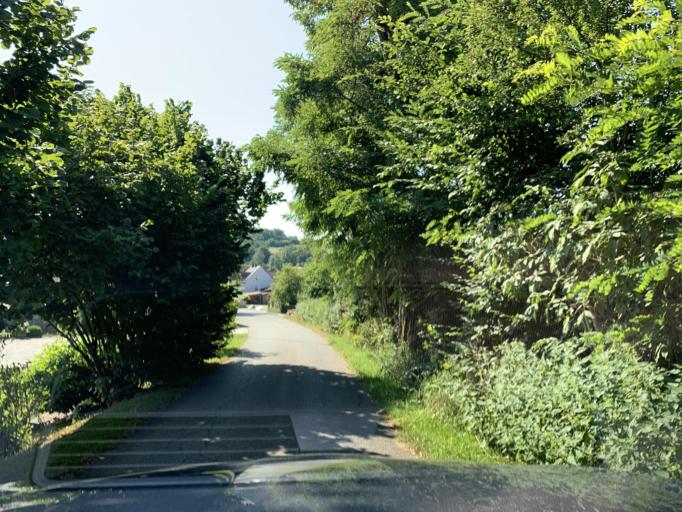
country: DE
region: Bavaria
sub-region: Upper Palatinate
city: Altendorf
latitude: 49.3986
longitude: 12.3066
